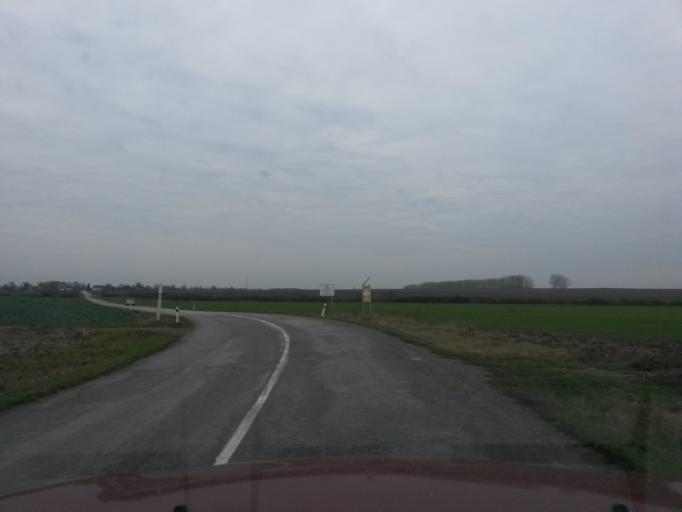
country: SK
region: Kosicky
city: Trebisov
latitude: 48.6288
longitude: 21.6520
